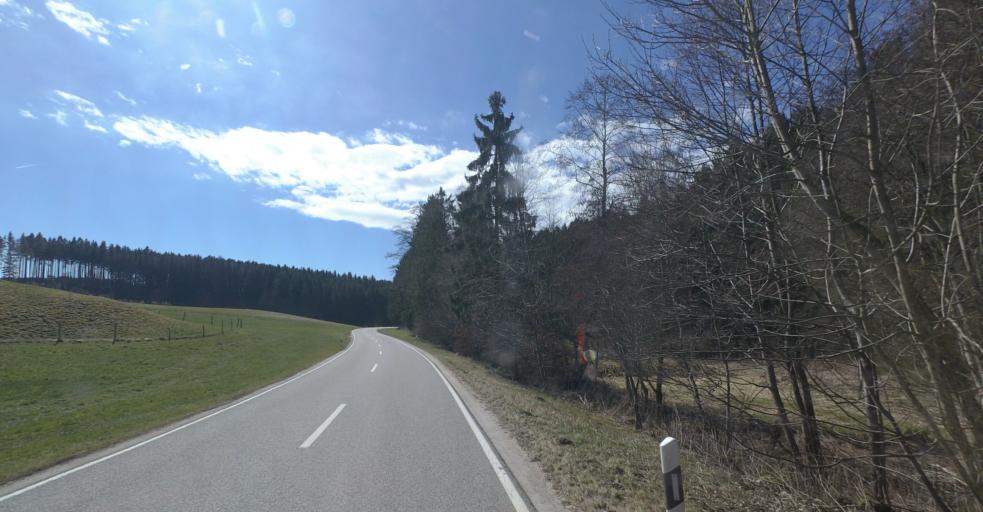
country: DE
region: Bavaria
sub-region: Upper Bavaria
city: Chieming
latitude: 47.9415
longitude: 12.5426
